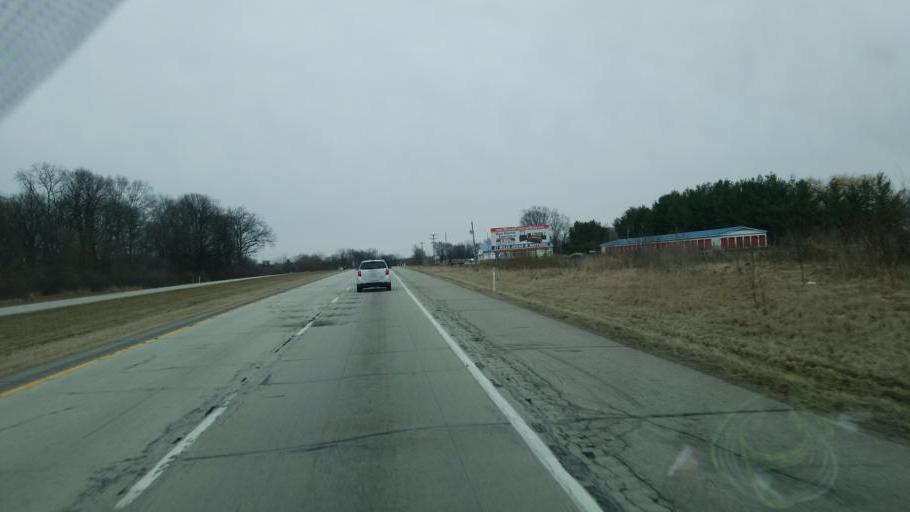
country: US
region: Indiana
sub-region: Marshall County
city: Plymouth
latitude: 41.3645
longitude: -86.3903
